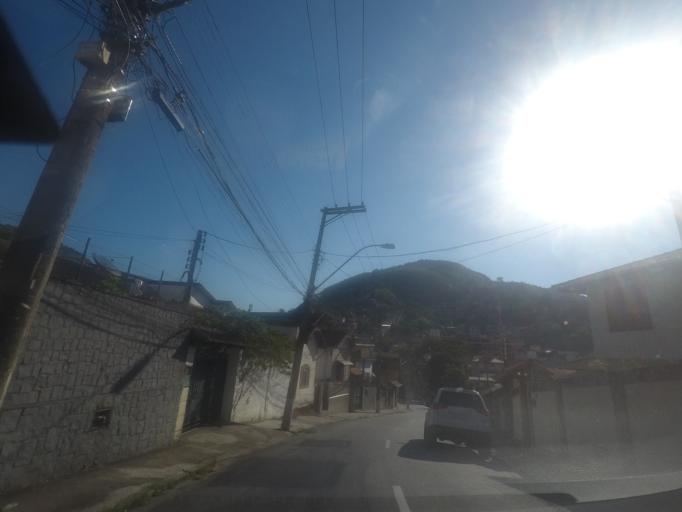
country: BR
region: Rio de Janeiro
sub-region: Petropolis
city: Petropolis
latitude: -22.5154
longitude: -43.1681
